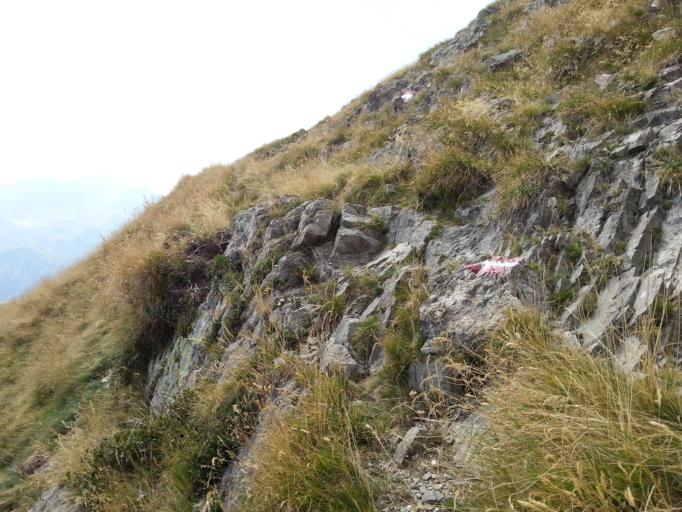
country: CH
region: Grisons
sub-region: Moesa District
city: Roveredo
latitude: 46.1681
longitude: 9.1735
